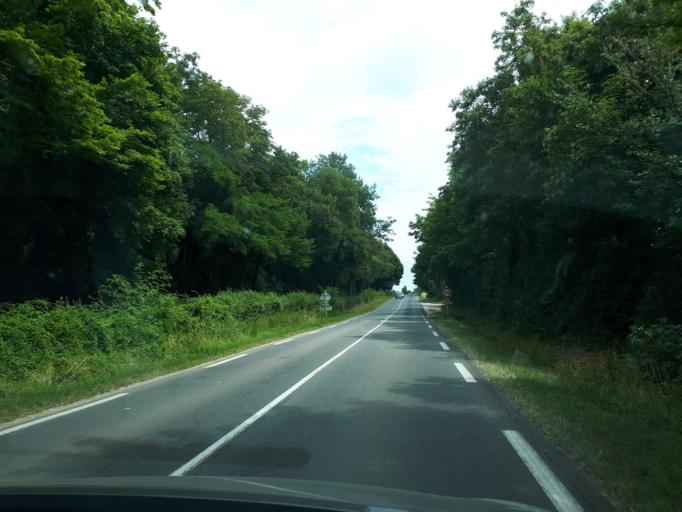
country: FR
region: Centre
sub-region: Departement du Cher
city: Rians
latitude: 47.2230
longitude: 2.6323
